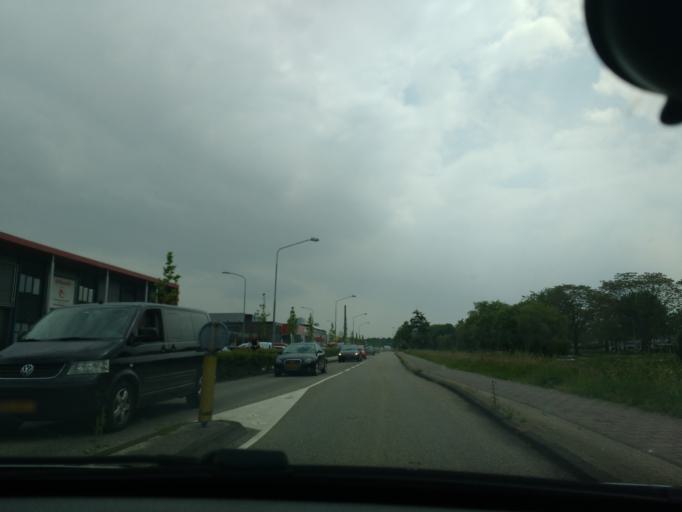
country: NL
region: North Holland
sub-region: Gemeente Naarden
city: Naarden
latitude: 52.3026
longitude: 5.1462
